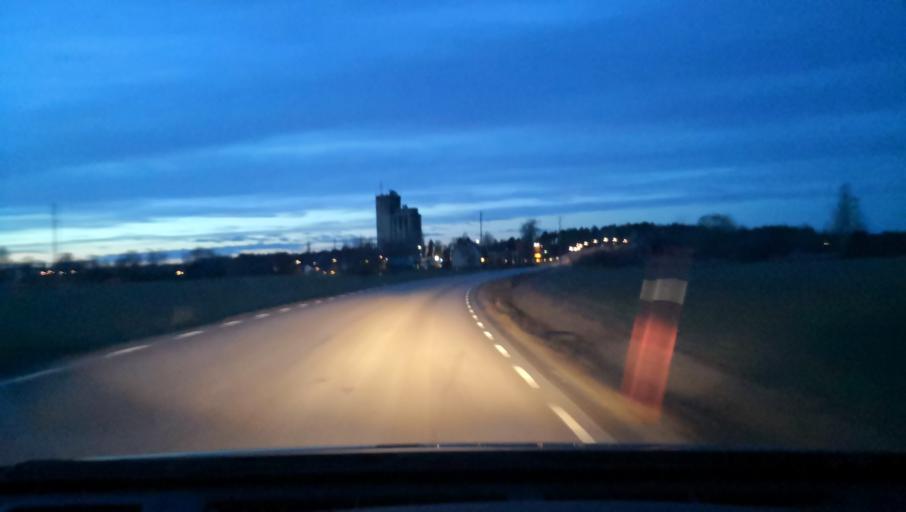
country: SE
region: Uppsala
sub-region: Enkopings Kommun
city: Grillby
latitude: 59.6198
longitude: 17.2629
